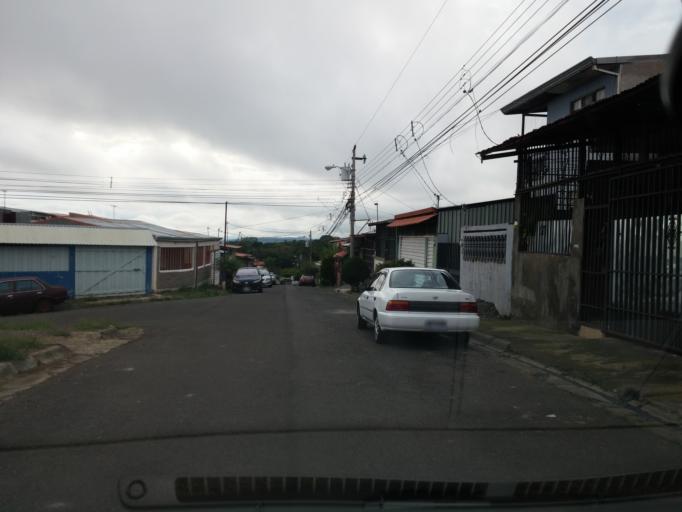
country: CR
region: Heredia
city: San Josecito
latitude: 10.0217
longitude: -84.1024
